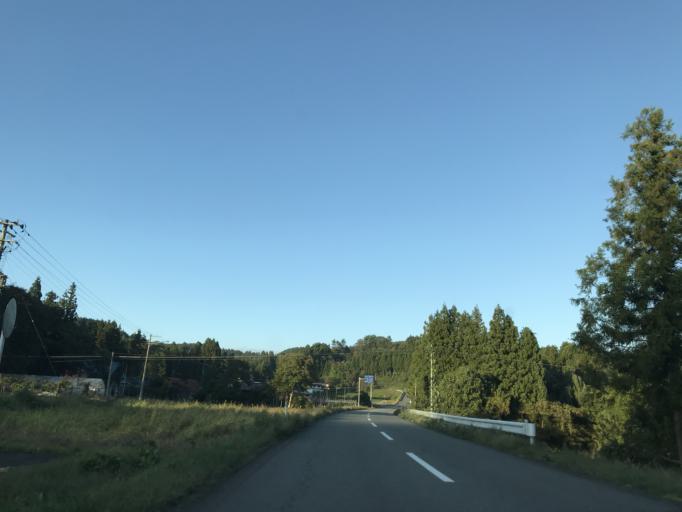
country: JP
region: Iwate
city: Mizusawa
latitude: 39.0519
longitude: 141.0430
